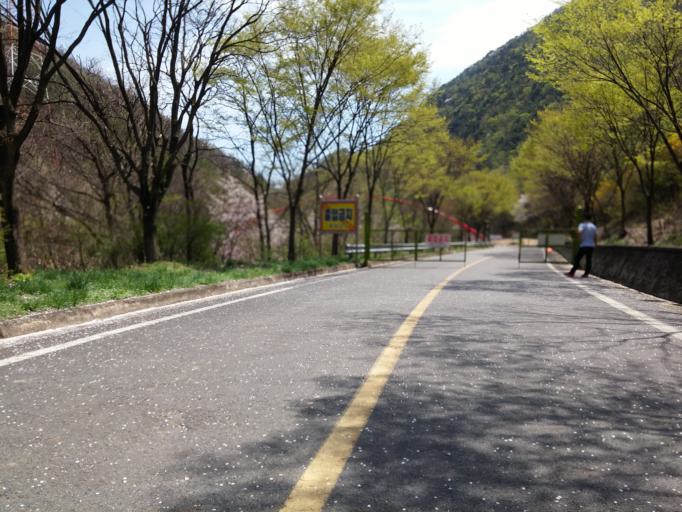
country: KR
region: Chungcheongbuk-do
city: Okcheon
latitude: 36.2409
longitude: 127.5555
